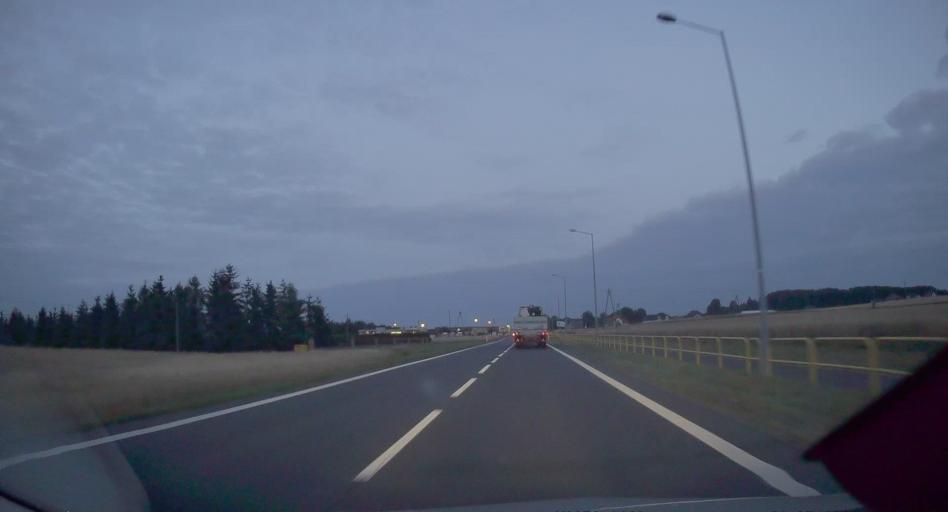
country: PL
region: Silesian Voivodeship
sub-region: Powiat klobucki
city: Opatow
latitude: 50.9320
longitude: 18.8561
